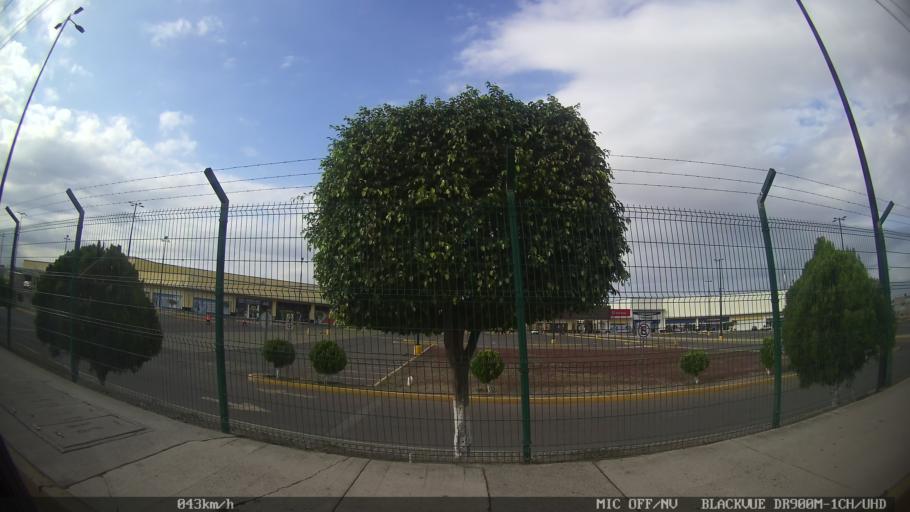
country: MX
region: Jalisco
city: Tlaquepaque
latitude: 20.6773
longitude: -103.2571
